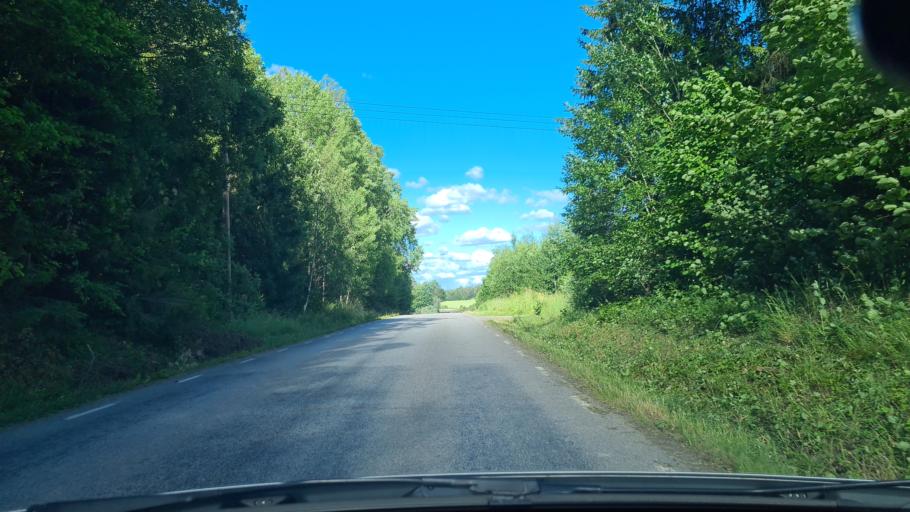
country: SE
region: Soedermanland
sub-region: Nykopings Kommun
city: Olstorp
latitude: 58.8218
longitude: 16.4972
